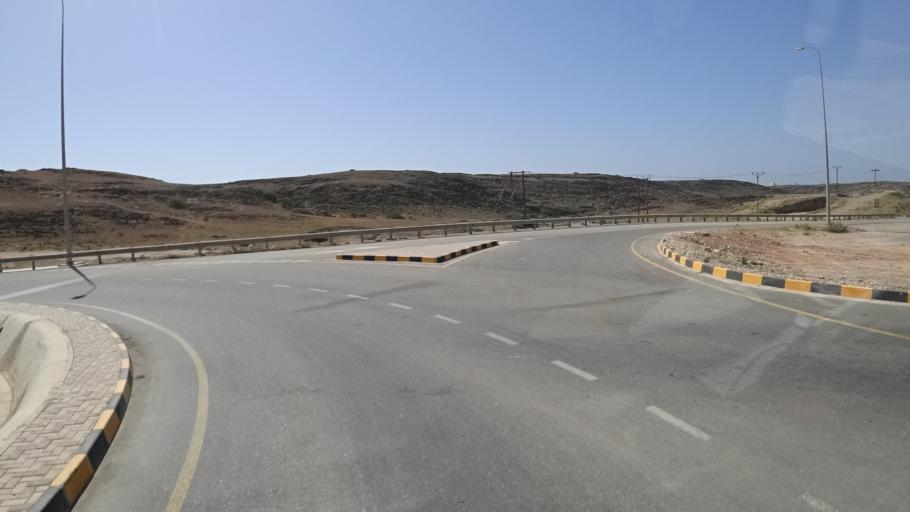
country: OM
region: Zufar
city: Salalah
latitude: 17.0586
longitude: 54.4319
